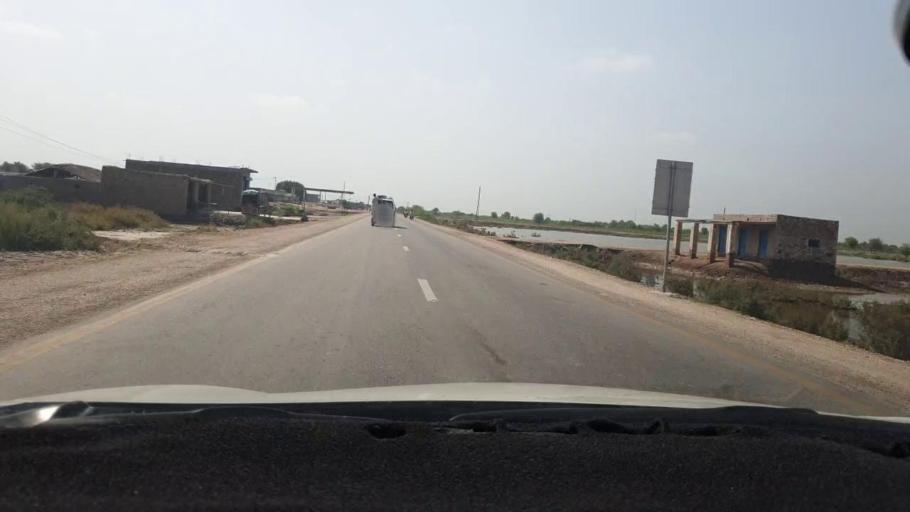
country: PK
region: Sindh
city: Mirpur Khas
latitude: 25.6121
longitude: 69.0829
